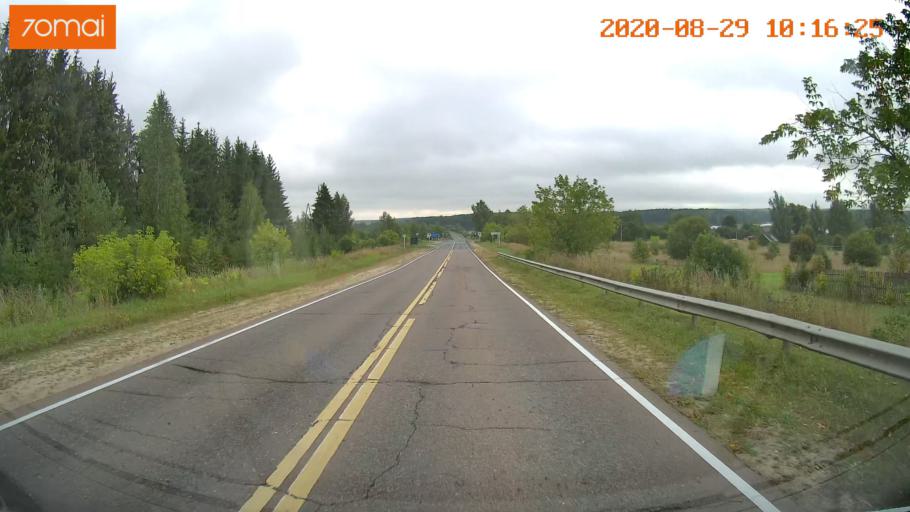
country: RU
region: Ivanovo
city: Yur'yevets
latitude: 57.3383
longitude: 42.7916
